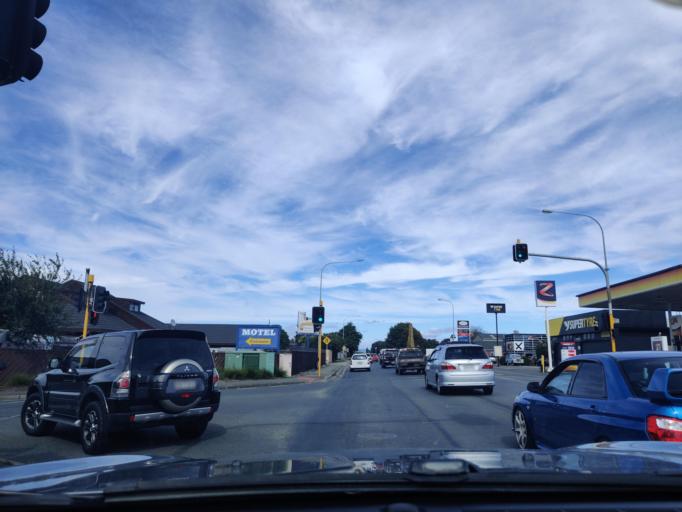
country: NZ
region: Tasman
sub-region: Tasman District
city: Richmond
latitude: -41.3374
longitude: 173.1806
